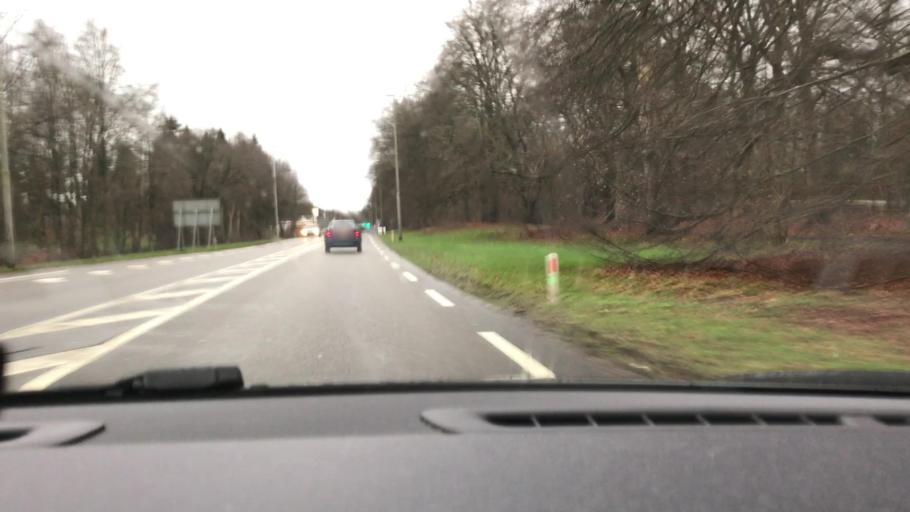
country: NL
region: Gelderland
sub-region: Gemeente Arnhem
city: Arnhem
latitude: 52.0064
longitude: 5.9244
